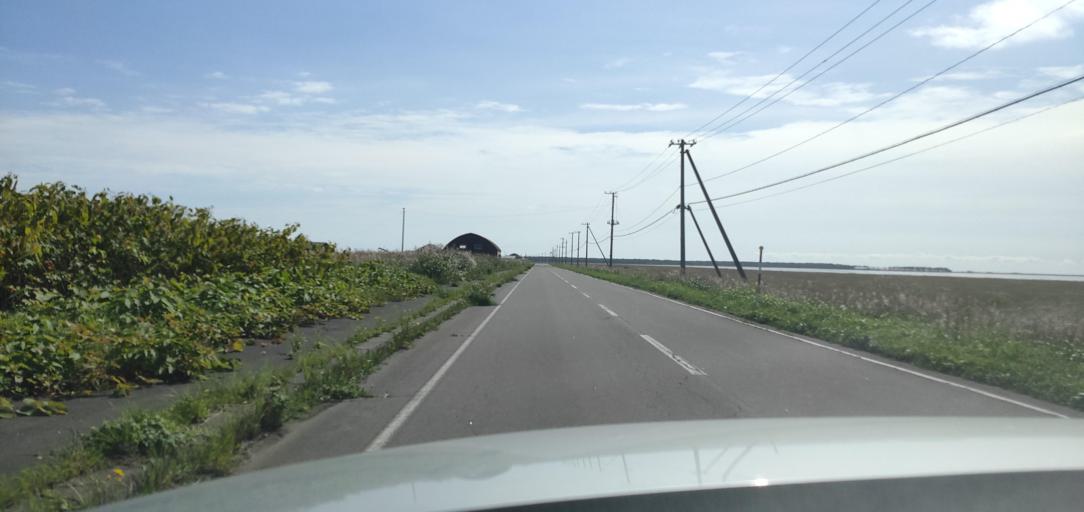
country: JP
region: Hokkaido
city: Shibetsu
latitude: 43.6182
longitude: 145.2331
